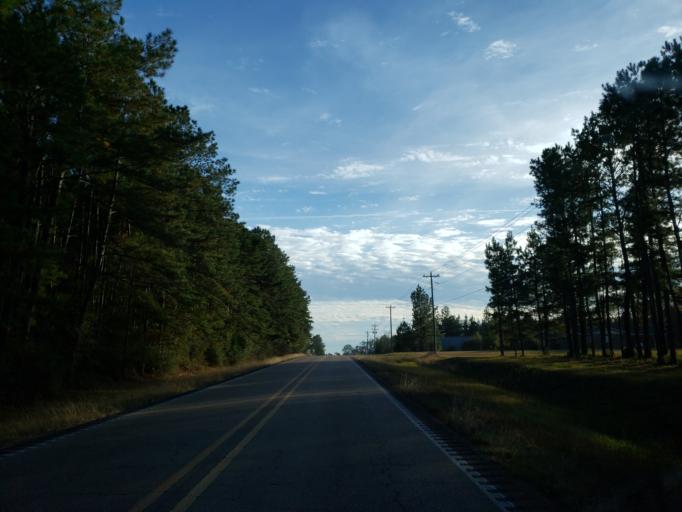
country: US
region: Mississippi
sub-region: Lamar County
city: West Hattiesburg
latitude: 31.2747
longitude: -89.4656
